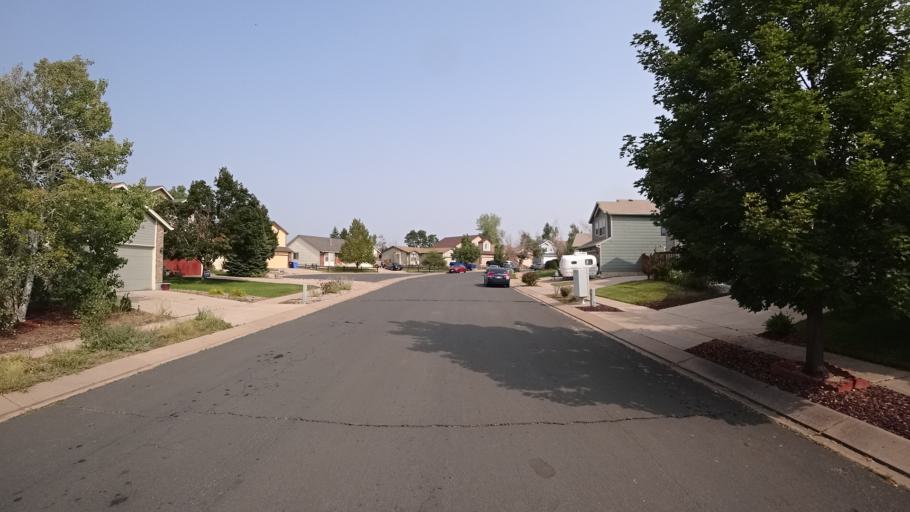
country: US
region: Colorado
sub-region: El Paso County
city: Cimarron Hills
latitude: 38.9266
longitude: -104.7308
